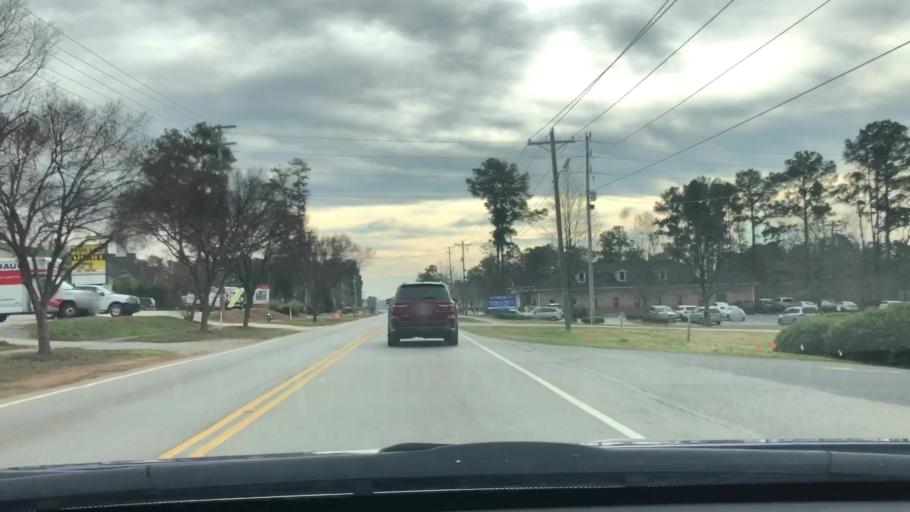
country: US
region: South Carolina
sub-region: Lexington County
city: Irmo
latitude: 34.1065
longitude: -81.1885
